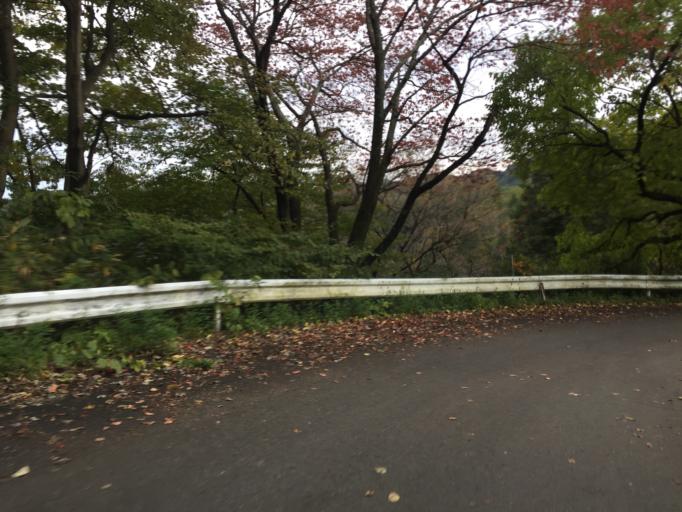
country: JP
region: Fukushima
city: Hobaramachi
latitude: 37.7743
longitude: 140.5347
